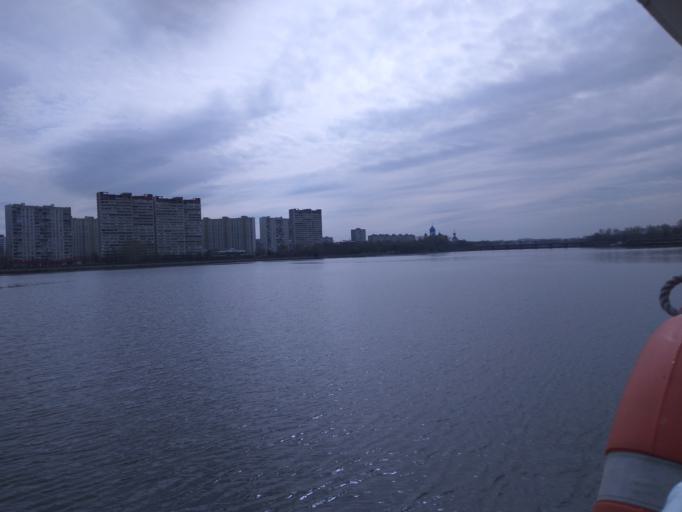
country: RU
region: Moscow
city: Kolomenskoye
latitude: 55.6810
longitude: 37.7097
